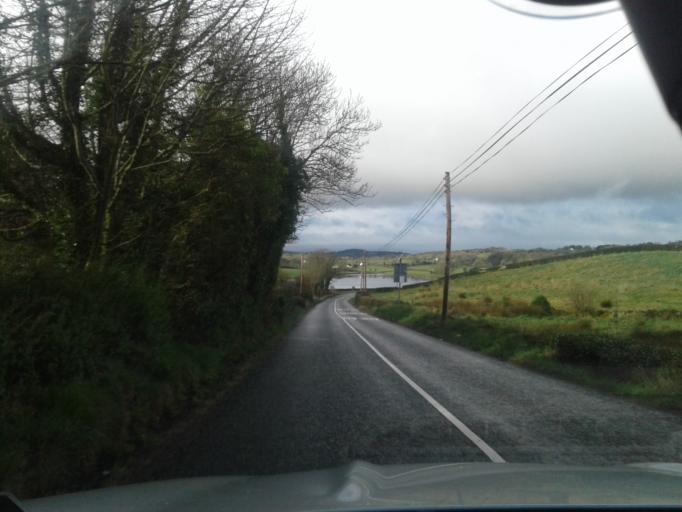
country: IE
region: Ulster
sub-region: County Donegal
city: Ramelton
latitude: 55.0601
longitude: -7.6230
